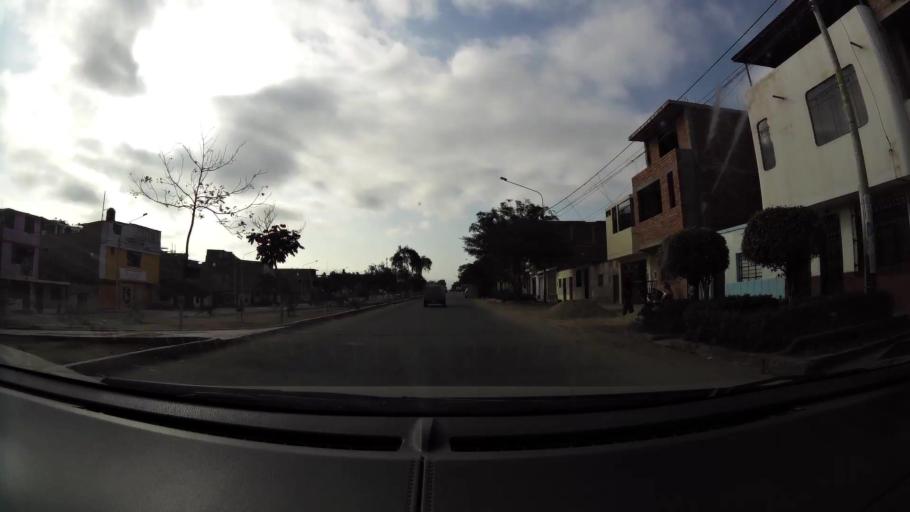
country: PE
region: La Libertad
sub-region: Provincia de Trujillo
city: La Esperanza
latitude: -8.0792
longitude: -79.0435
